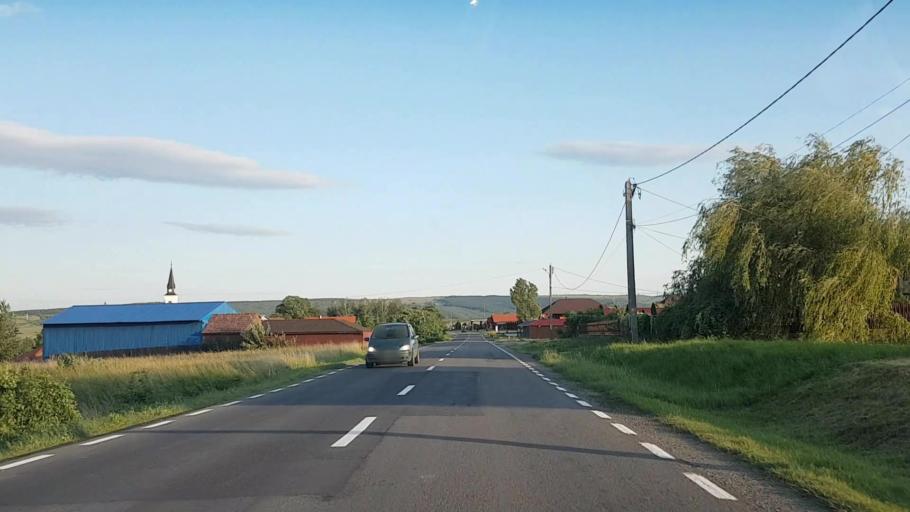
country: RO
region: Harghita
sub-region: Comuna Lupeni
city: Lupeni
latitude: 46.3803
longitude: 25.2193
